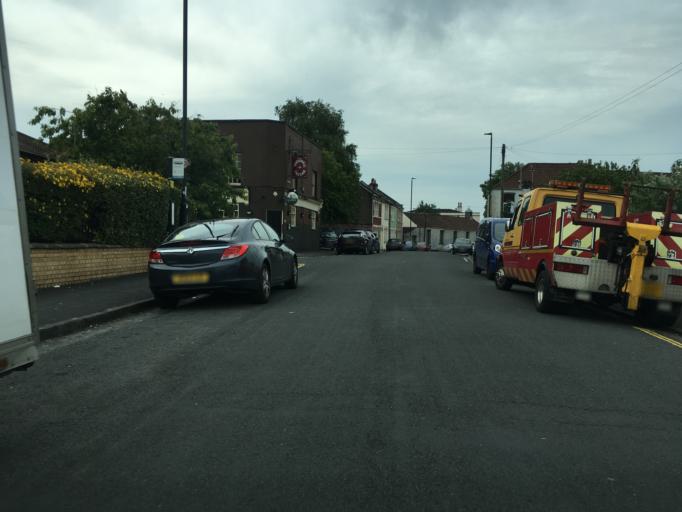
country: GB
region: England
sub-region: Bristol
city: Bristol
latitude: 51.4632
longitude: -2.5575
